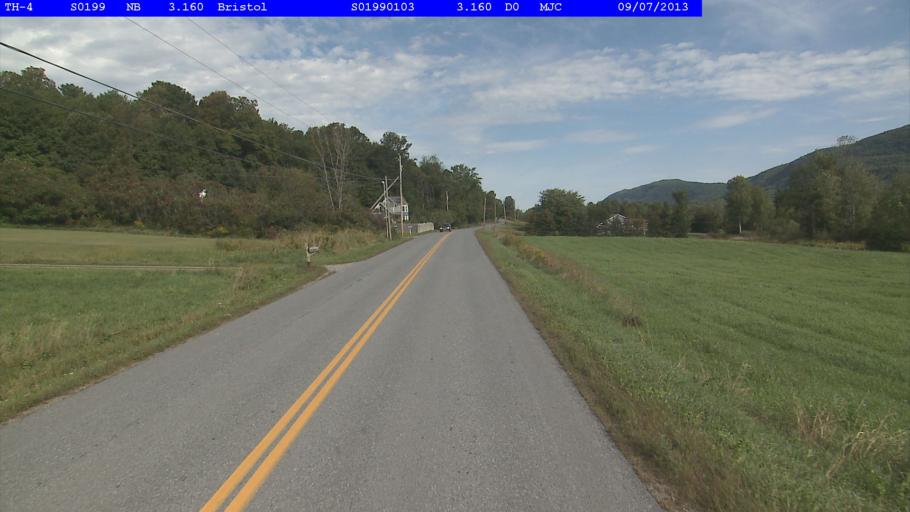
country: US
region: Vermont
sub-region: Addison County
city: Bristol
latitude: 44.1737
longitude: -73.1021
